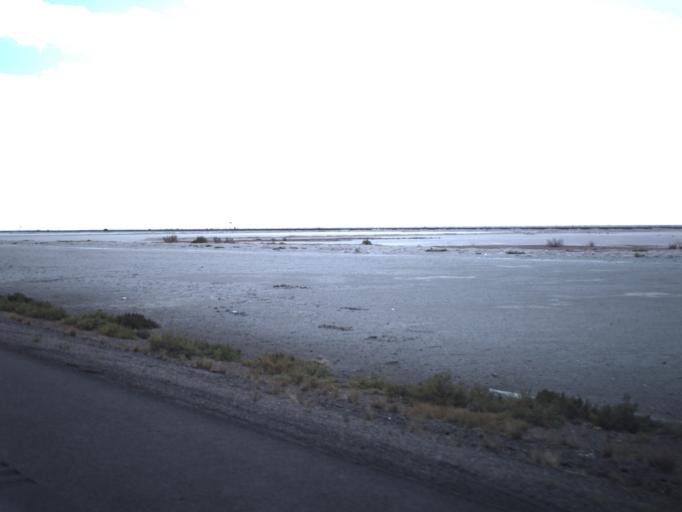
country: US
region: Utah
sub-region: Tooele County
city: Wendover
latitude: 40.7411
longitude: -113.9601
